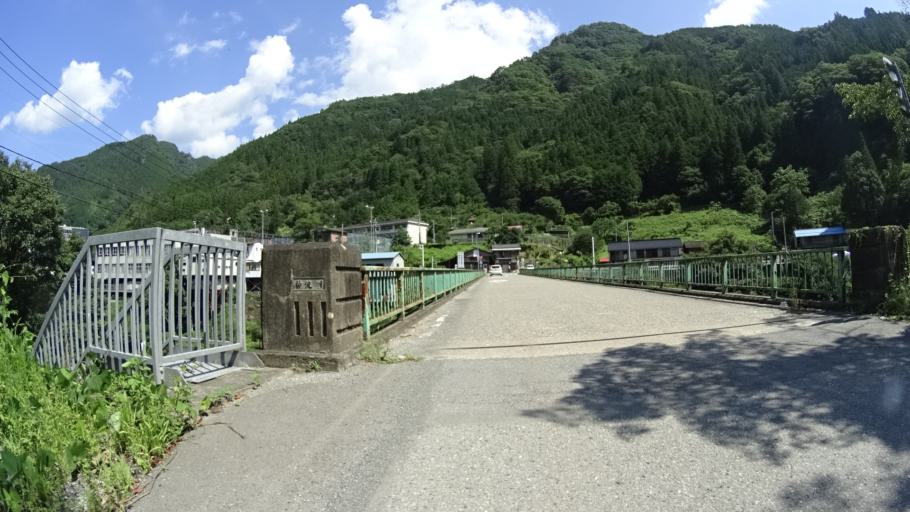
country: JP
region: Gunma
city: Tomioka
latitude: 36.0903
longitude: 138.8290
